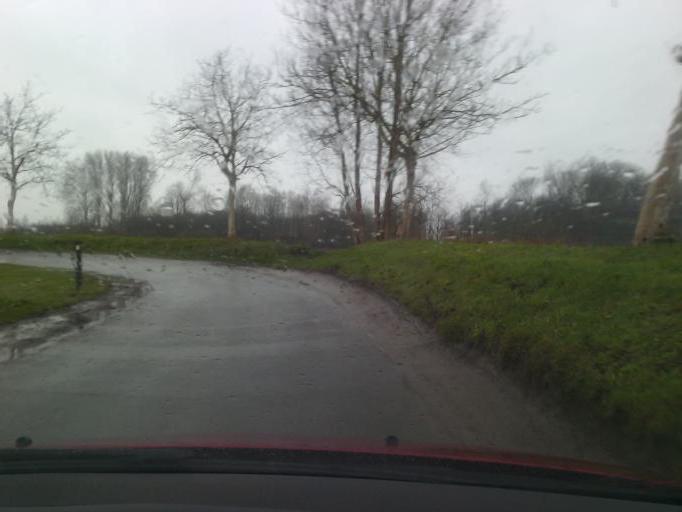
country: BE
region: Flanders
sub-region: Provincie Oost-Vlaanderen
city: Wichelen
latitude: 51.0208
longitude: 3.9803
